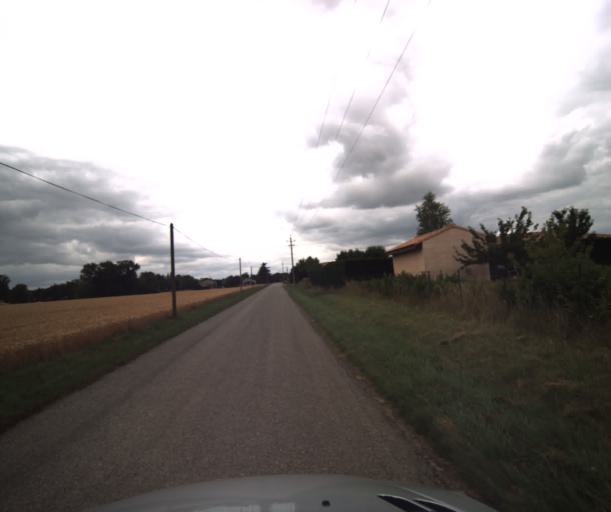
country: FR
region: Midi-Pyrenees
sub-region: Departement de la Haute-Garonne
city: Labarthe-sur-Leze
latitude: 43.4594
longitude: 1.4068
